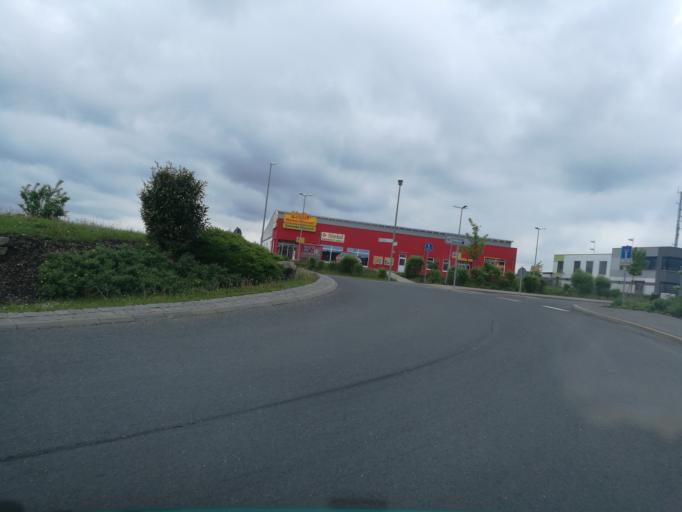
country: DE
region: Bavaria
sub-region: Upper Franconia
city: Niederfullbach
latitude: 50.2222
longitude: 11.0569
